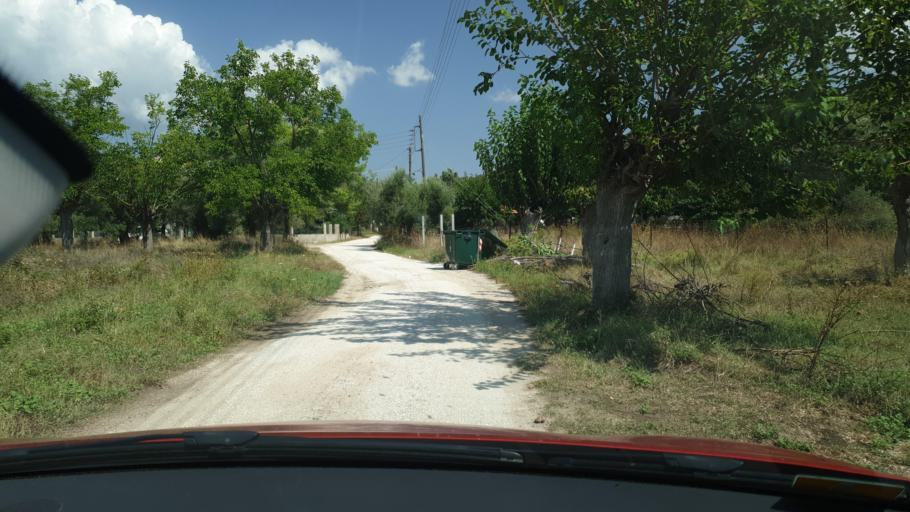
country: GR
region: Central Macedonia
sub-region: Nomos Chalkidikis
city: Sykia
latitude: 39.9805
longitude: 23.9089
